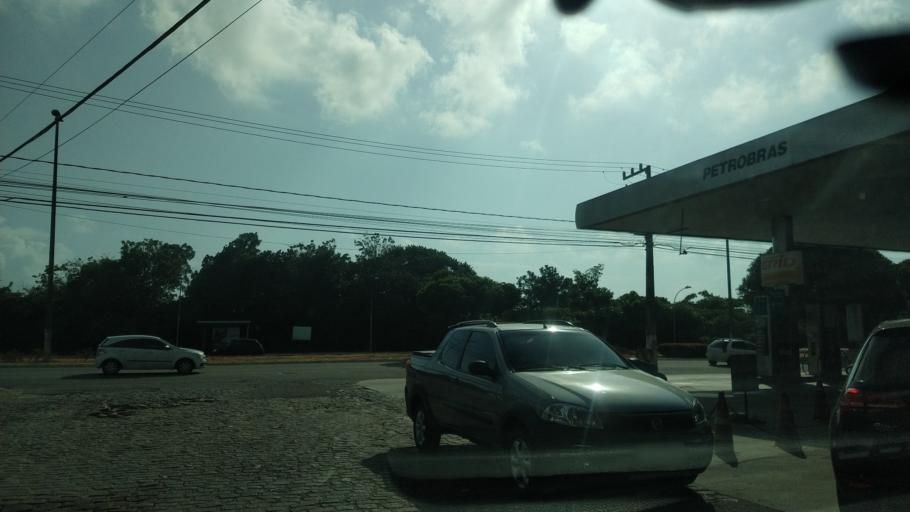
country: BR
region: Rio Grande do Norte
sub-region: Natal
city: Natal
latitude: -5.8554
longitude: -35.1999
